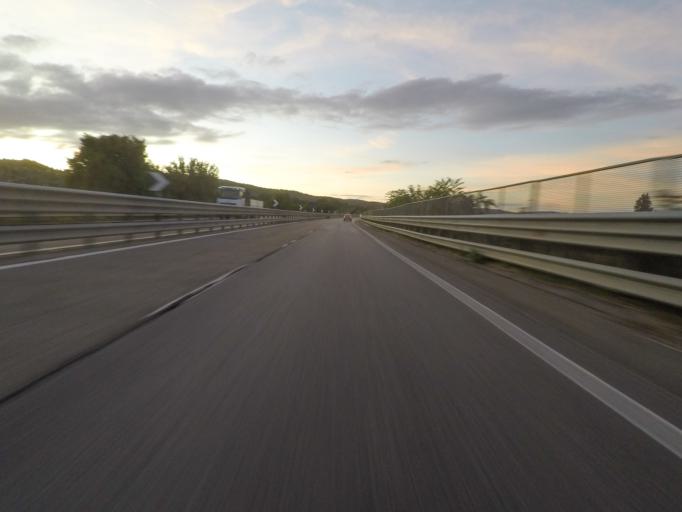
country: IT
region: Tuscany
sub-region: Provincia di Siena
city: Sinalunga
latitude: 43.2292
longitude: 11.7333
